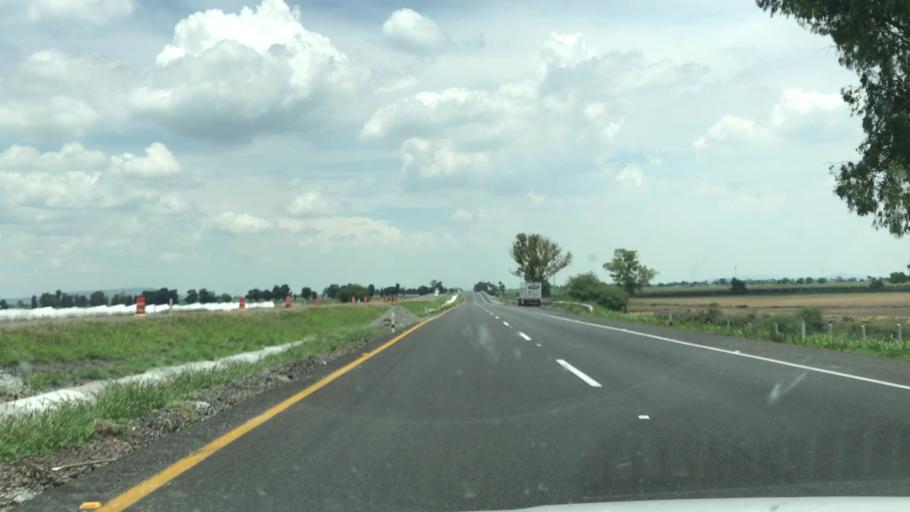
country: MX
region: Guanajuato
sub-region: Salamanca
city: San Vicente de Flores
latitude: 20.6389
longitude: -101.2632
